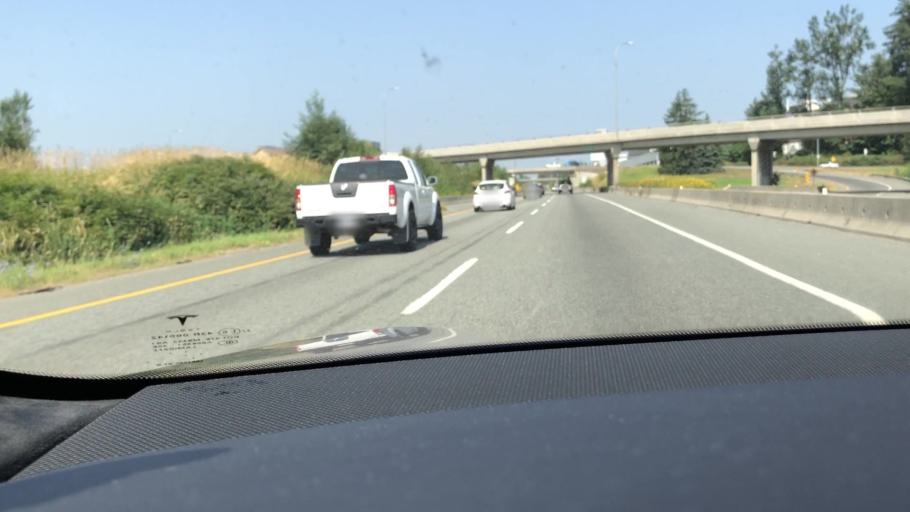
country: CA
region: British Columbia
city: Aldergrove
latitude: 49.0554
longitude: -122.3751
